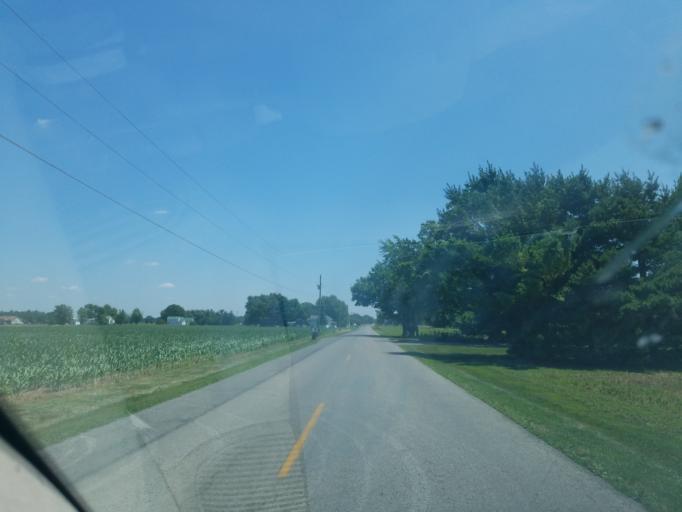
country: US
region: Ohio
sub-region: Allen County
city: Elida
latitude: 40.7874
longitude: -84.2478
